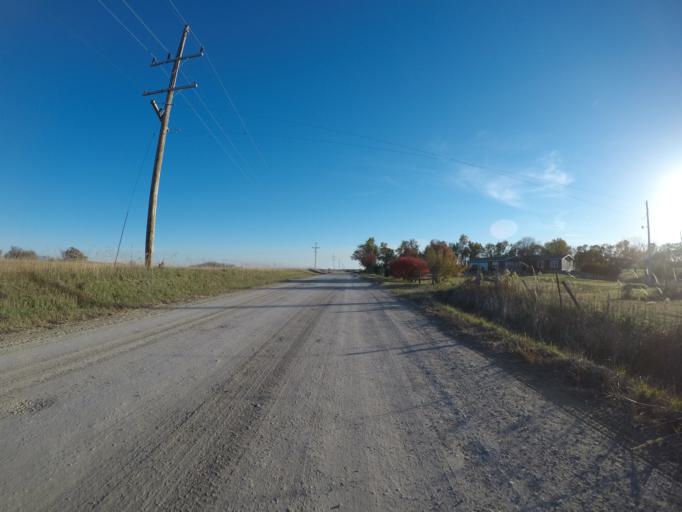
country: US
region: Kansas
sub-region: Riley County
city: Manhattan
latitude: 39.2553
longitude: -96.6819
